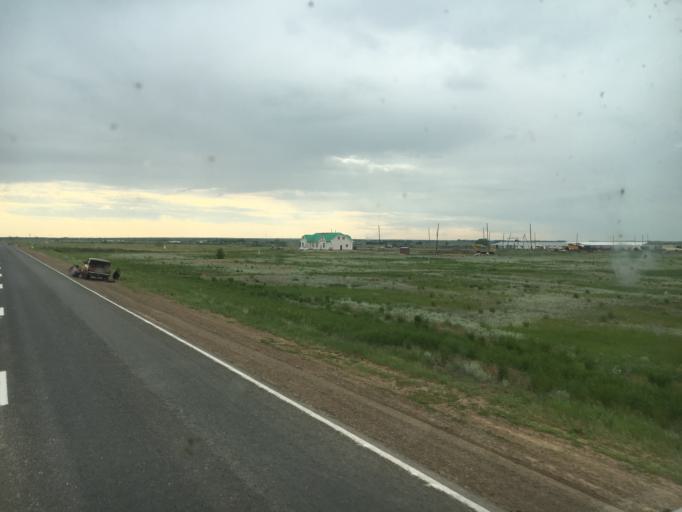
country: KZ
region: Batys Qazaqstan
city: Oral
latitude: 51.1229
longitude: 51.4552
